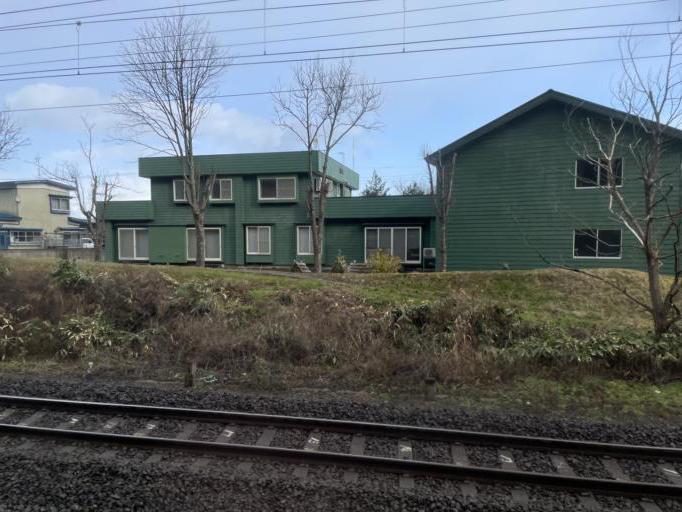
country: JP
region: Aomori
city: Aomori Shi
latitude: 40.9229
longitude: 141.0226
